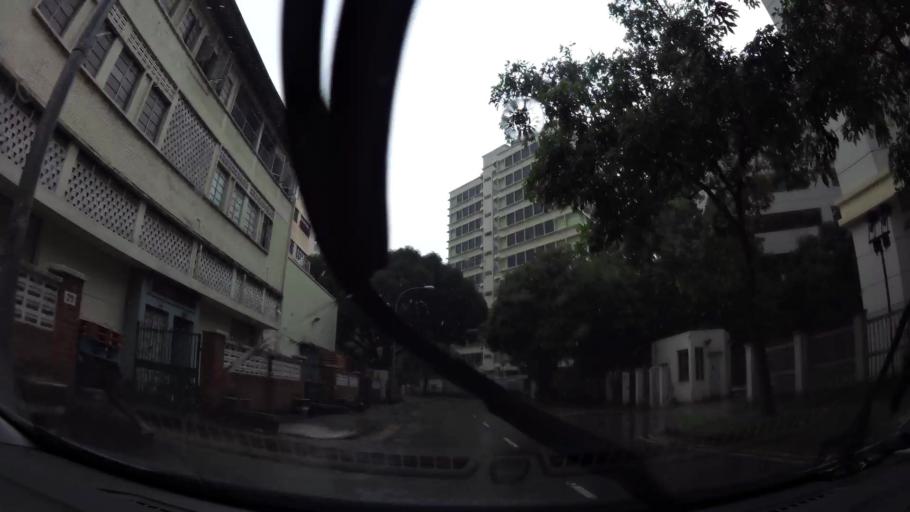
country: SG
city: Singapore
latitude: 1.3345
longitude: 103.8841
